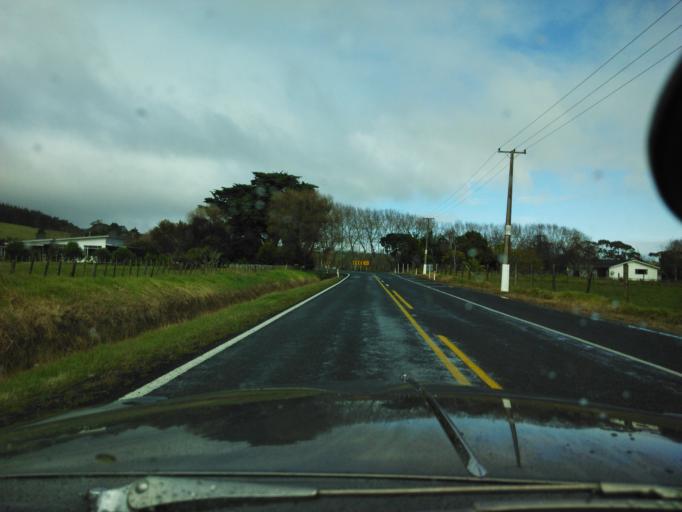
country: NZ
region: Auckland
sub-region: Auckland
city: Parakai
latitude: -36.4948
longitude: 174.4485
